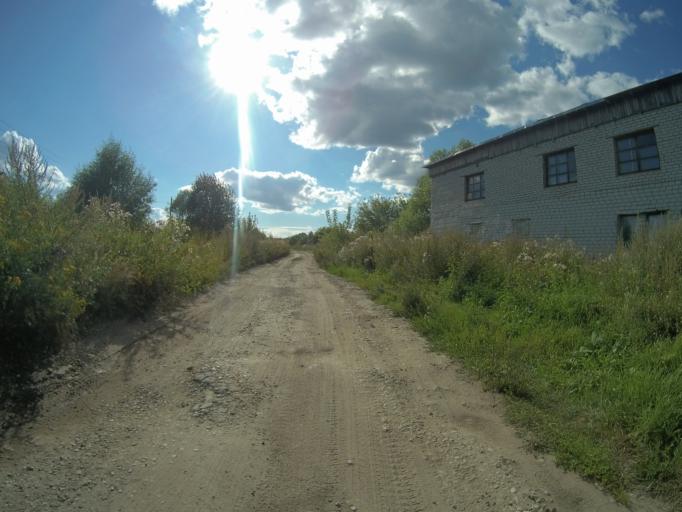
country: RU
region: Vladimir
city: Vladimir
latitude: 56.1659
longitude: 40.4056
